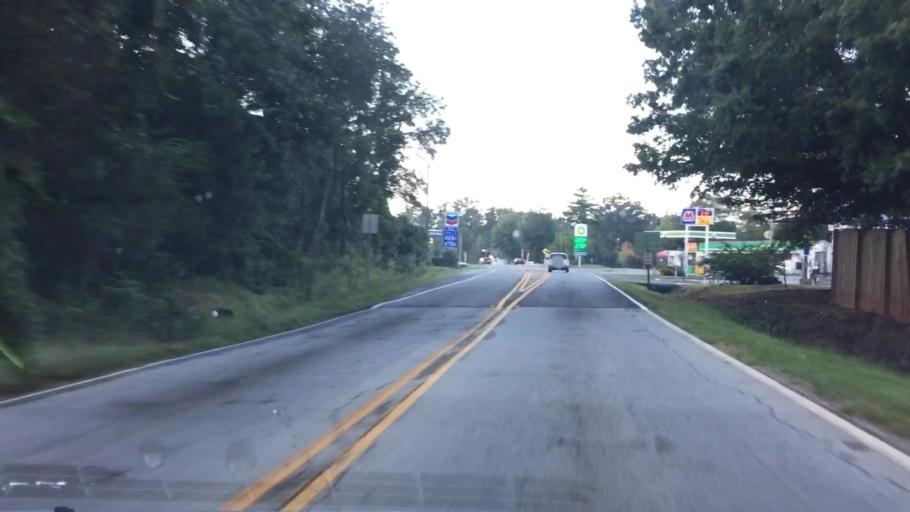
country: US
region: Georgia
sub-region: Clayton County
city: Lovejoy
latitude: 33.4239
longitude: -84.2847
